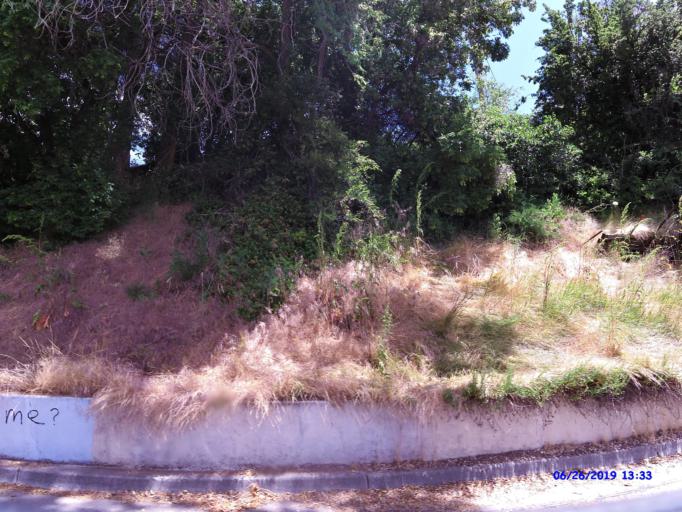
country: US
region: Utah
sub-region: Weber County
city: South Ogden
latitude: 41.2055
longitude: -111.9625
